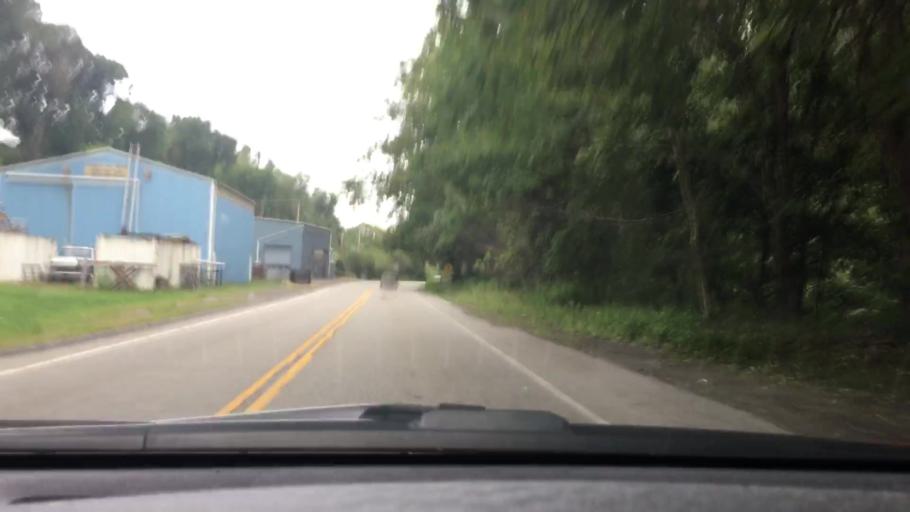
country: US
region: Pennsylvania
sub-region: Allegheny County
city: Glassport
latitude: 40.3211
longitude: -79.9014
